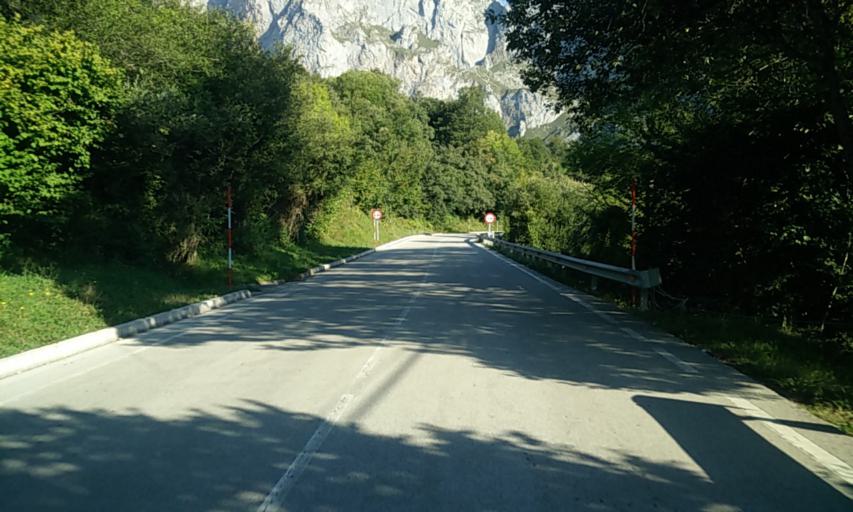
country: ES
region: Castille and Leon
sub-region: Provincia de Leon
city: Posada de Valdeon
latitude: 43.1370
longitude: -4.8107
